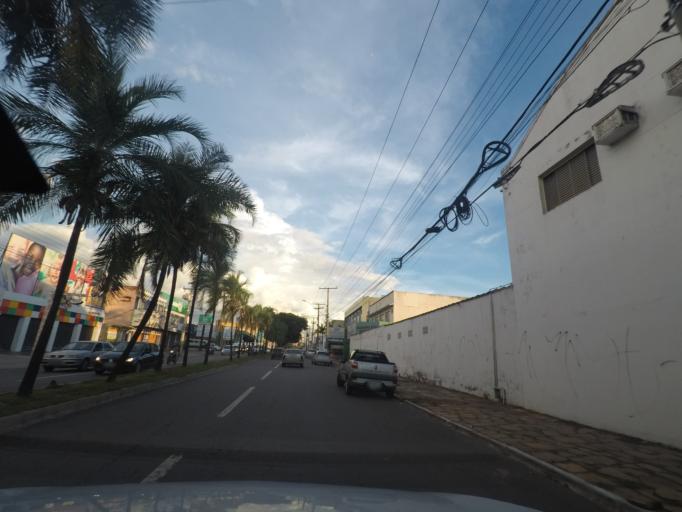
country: BR
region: Goias
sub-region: Goiania
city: Goiania
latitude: -16.6795
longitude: -49.2849
